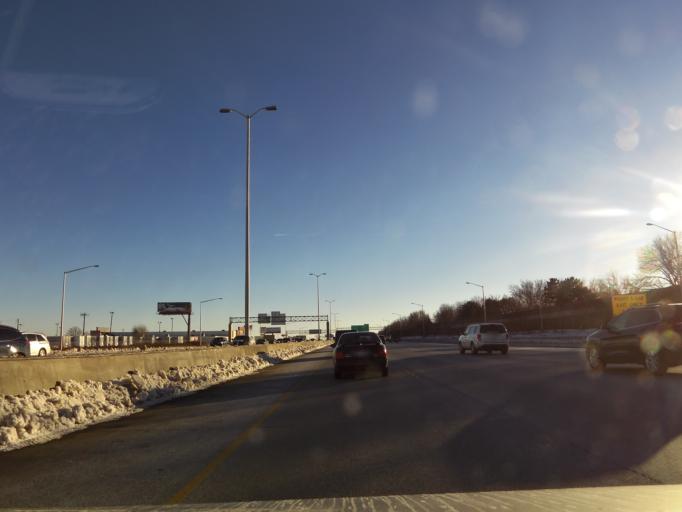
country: US
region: Wisconsin
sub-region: Milwaukee County
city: Greendale
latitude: 42.9276
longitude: -87.9354
